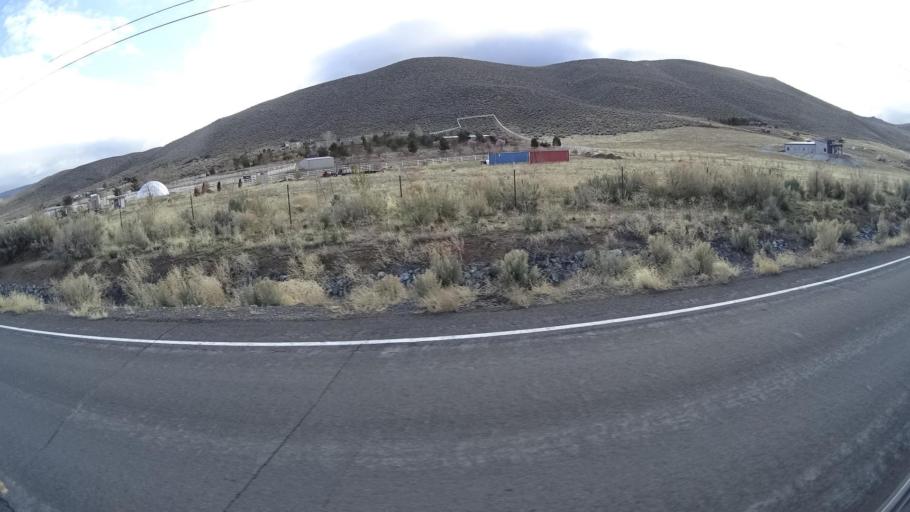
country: US
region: Nevada
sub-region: Carson City
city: Carson City
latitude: 39.2670
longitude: -119.7567
